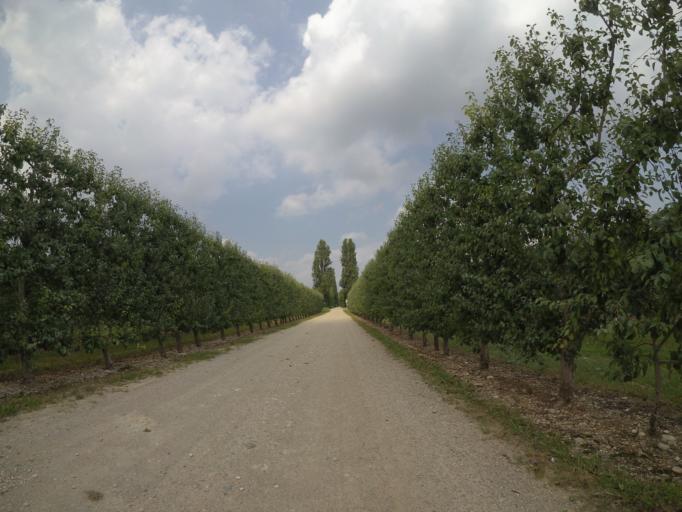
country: IT
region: Friuli Venezia Giulia
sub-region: Provincia di Udine
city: Sedegliano
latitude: 45.9971
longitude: 13.0108
